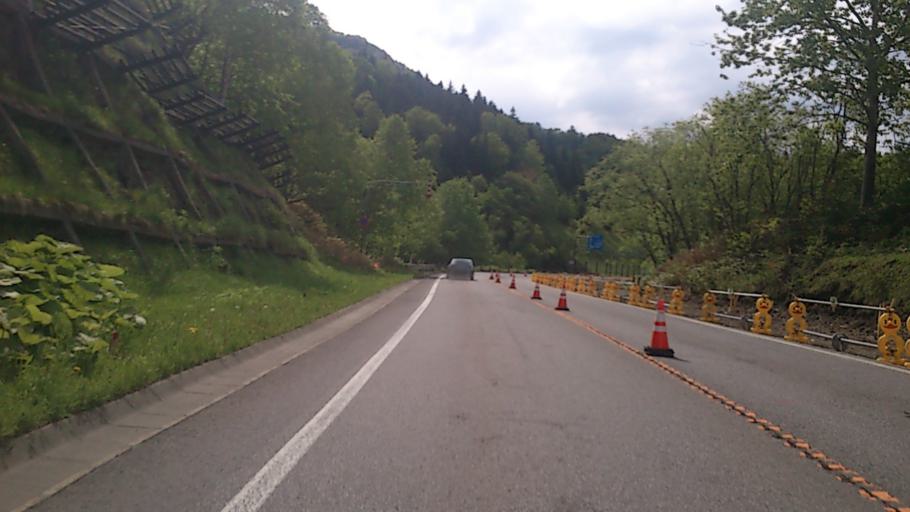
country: JP
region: Hokkaido
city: Kamikawa
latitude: 43.6833
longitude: 143.0337
